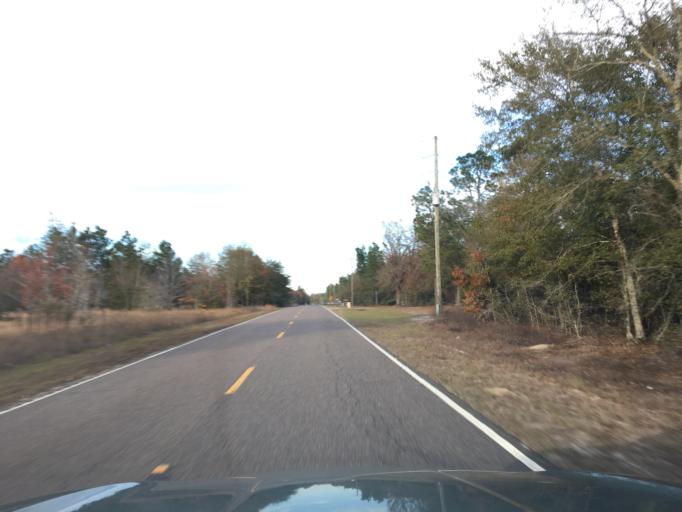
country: US
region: South Carolina
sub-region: Lexington County
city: Red Bank
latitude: 33.6970
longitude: -81.3601
